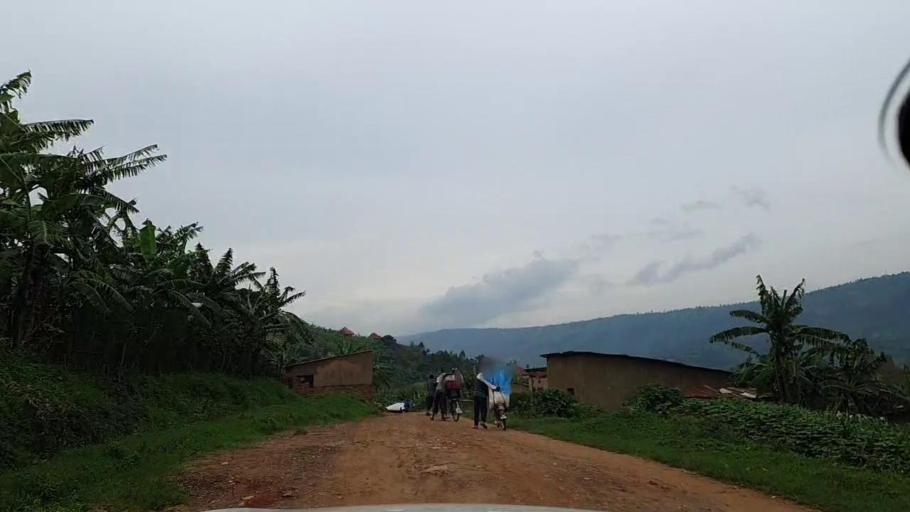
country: RW
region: Kigali
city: Kigali
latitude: -1.9455
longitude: 29.9892
